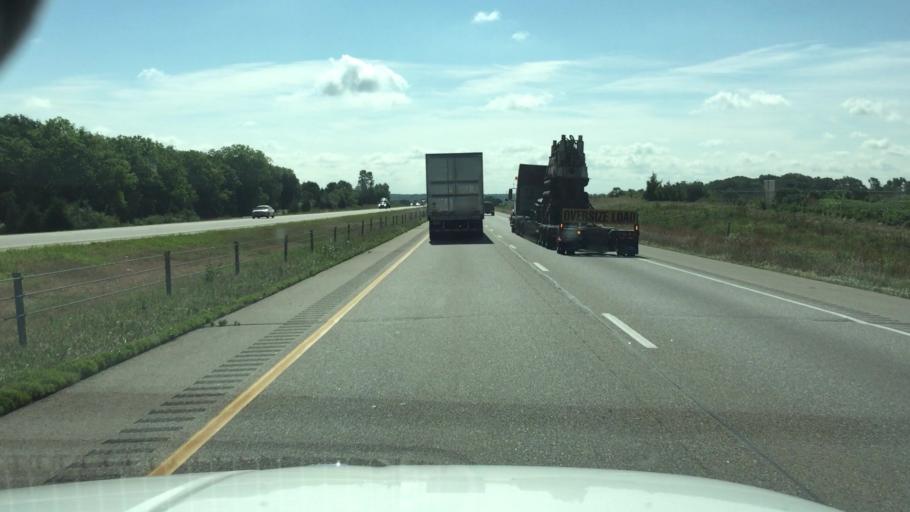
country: US
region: Iowa
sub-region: Muscatine County
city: West Liberty
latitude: 41.6492
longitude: -91.1741
